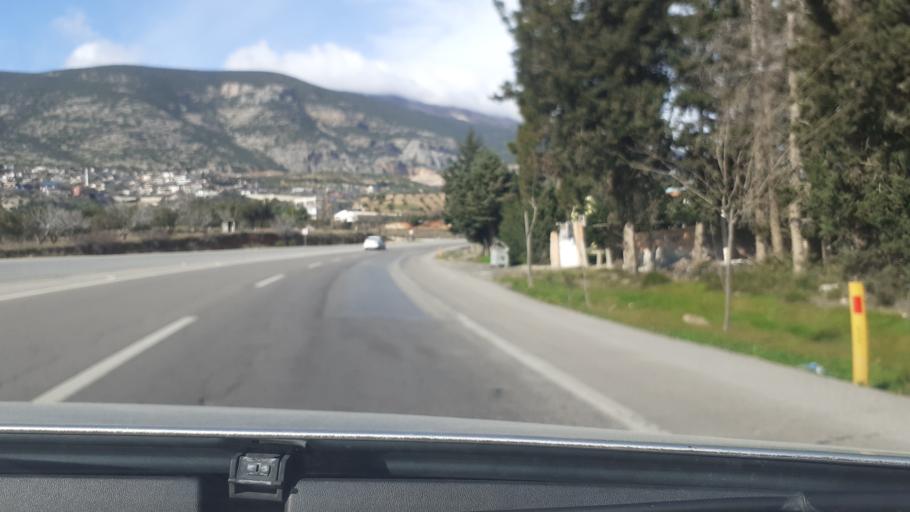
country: TR
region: Hatay
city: Belen
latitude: 36.4765
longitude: 36.2768
